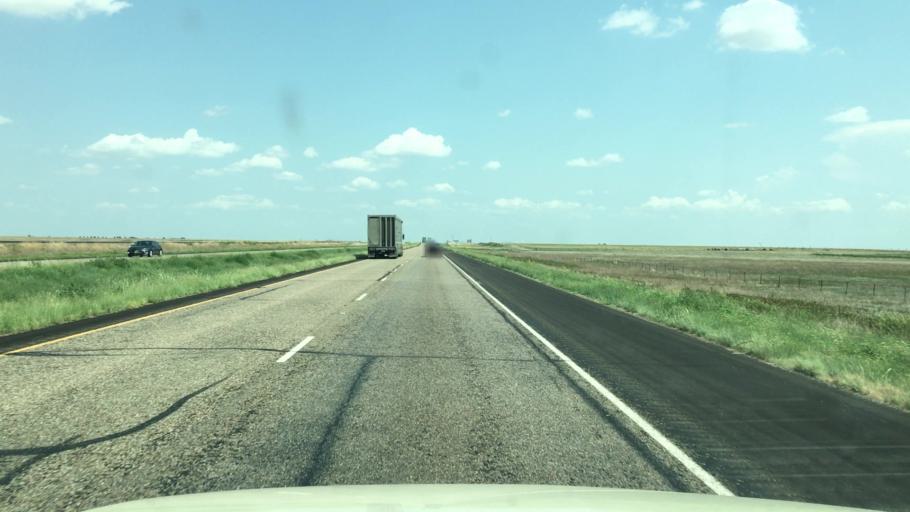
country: US
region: Texas
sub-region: Armstrong County
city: Claude
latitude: 35.1326
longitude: -101.4212
